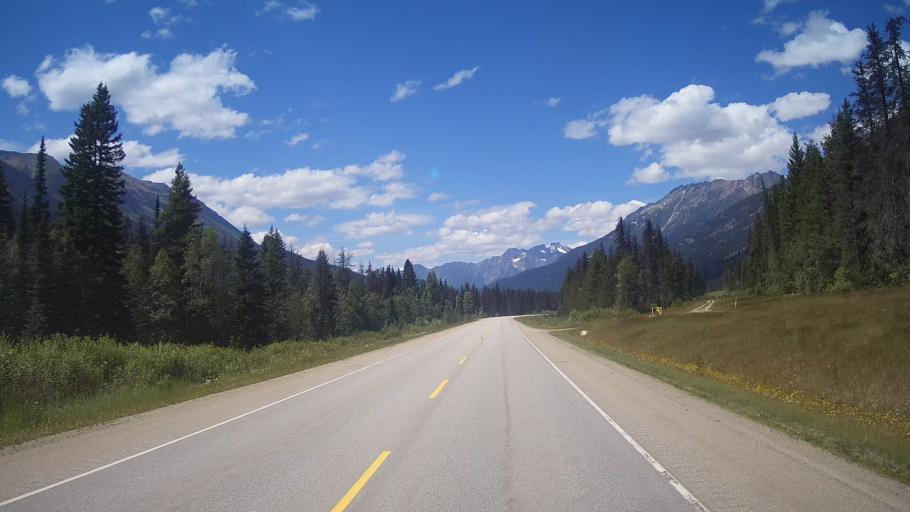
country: CA
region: Alberta
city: Grande Cache
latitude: 52.9894
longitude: -119.0067
